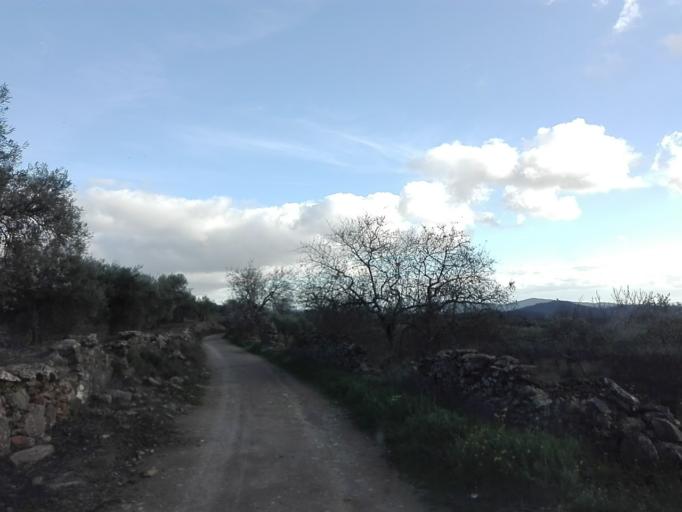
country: ES
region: Extremadura
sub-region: Provincia de Badajoz
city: Trasierra
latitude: 38.1874
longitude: -5.9901
